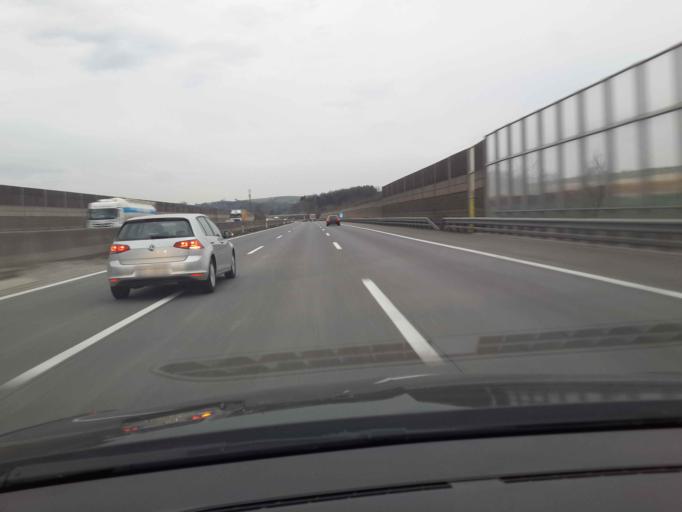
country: AT
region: Lower Austria
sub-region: Politischer Bezirk Melk
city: Blindenmarkt
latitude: 48.1326
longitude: 14.9938
